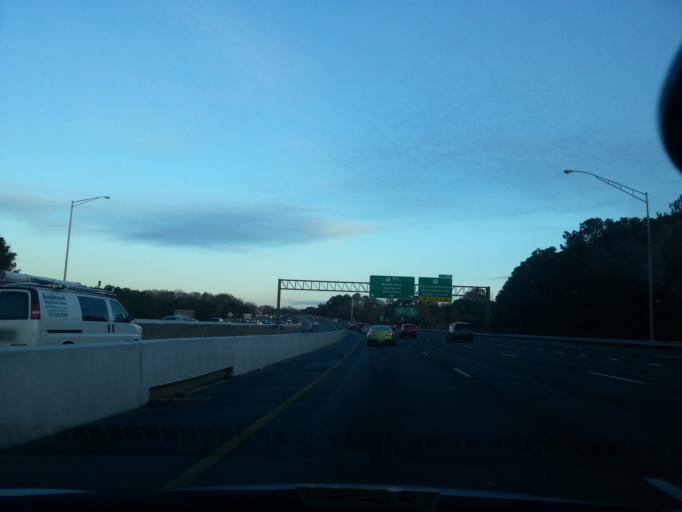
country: US
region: Virginia
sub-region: City of Norfolk
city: Norfolk
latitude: 36.8714
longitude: -76.1952
